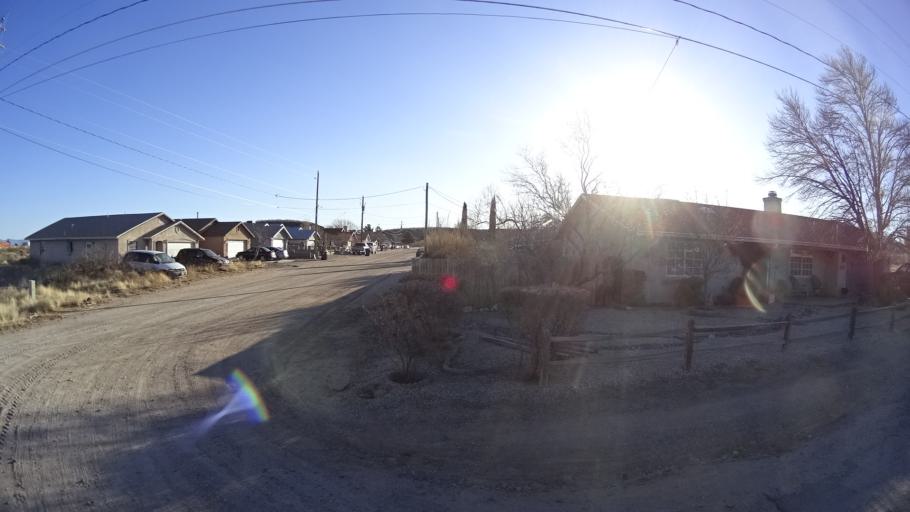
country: US
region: Arizona
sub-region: Mohave County
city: Kingman
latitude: 35.2069
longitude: -114.0136
